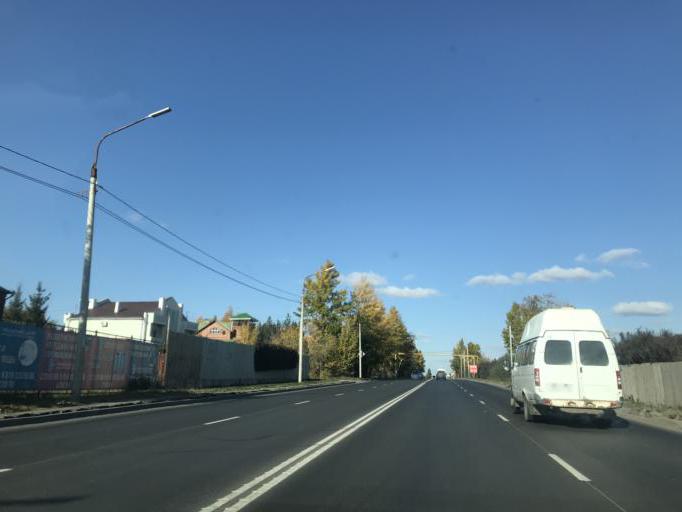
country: RU
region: Chelyabinsk
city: Roshchino
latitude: 55.2368
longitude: 61.3174
